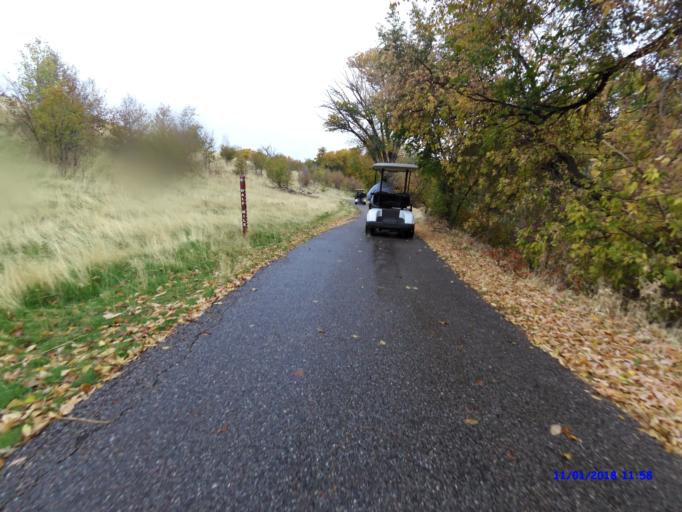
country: US
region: Utah
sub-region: Weber County
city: Ogden
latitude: 41.2351
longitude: -112.0001
